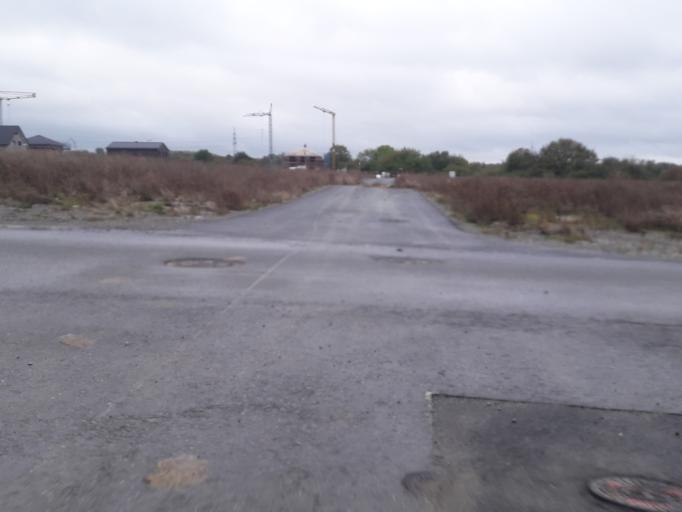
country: DE
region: North Rhine-Westphalia
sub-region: Regierungsbezirk Detmold
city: Paderborn
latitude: 51.7177
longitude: 8.8064
